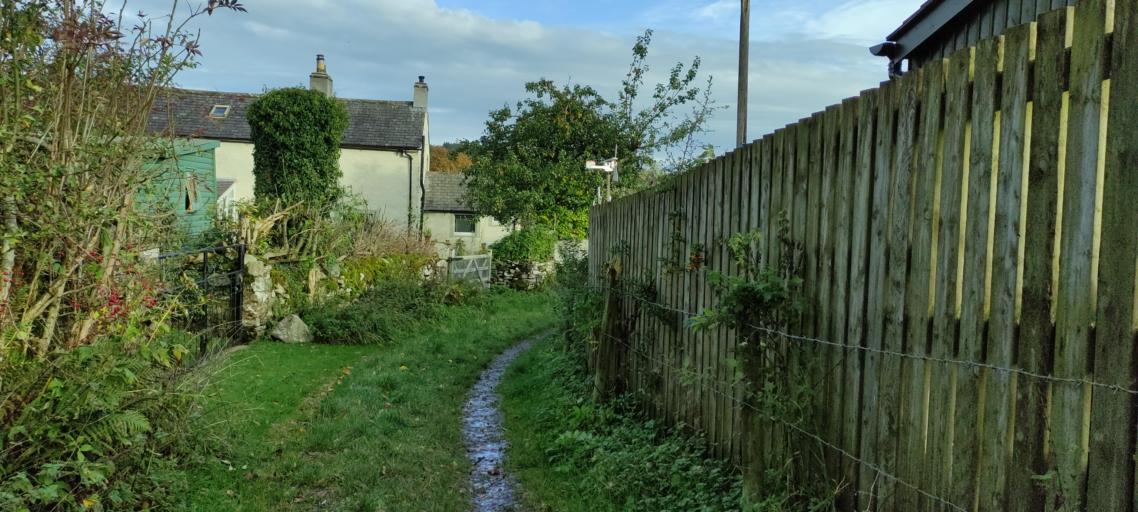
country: GB
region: England
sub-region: Cumbria
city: Wigton
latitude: 54.7502
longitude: -3.0572
